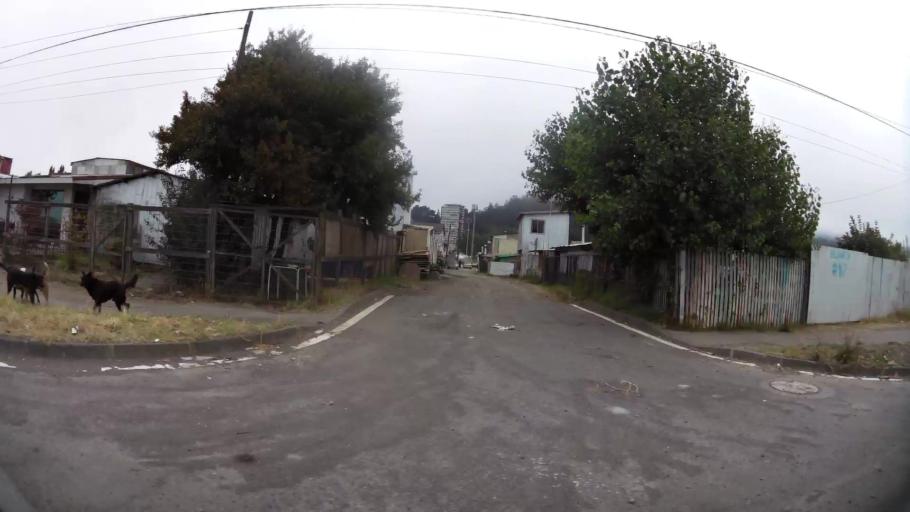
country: CL
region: Biobio
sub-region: Provincia de Concepcion
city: Concepcion
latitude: -36.8389
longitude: -73.0604
